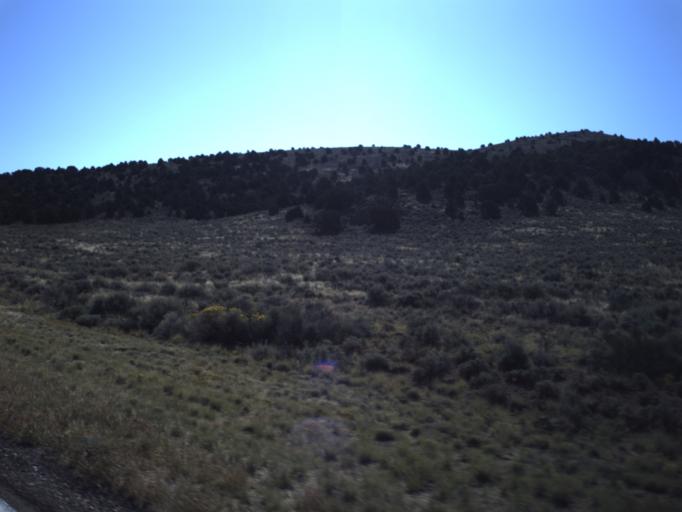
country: US
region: Utah
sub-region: Washington County
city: Enterprise
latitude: 37.6758
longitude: -113.5015
